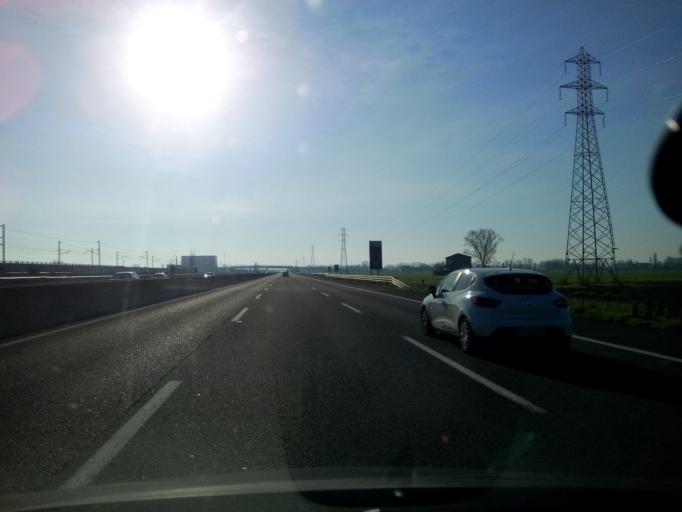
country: IT
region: Emilia-Romagna
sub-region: Provincia di Reggio Emilia
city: Prato
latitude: 44.6997
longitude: 10.7518
